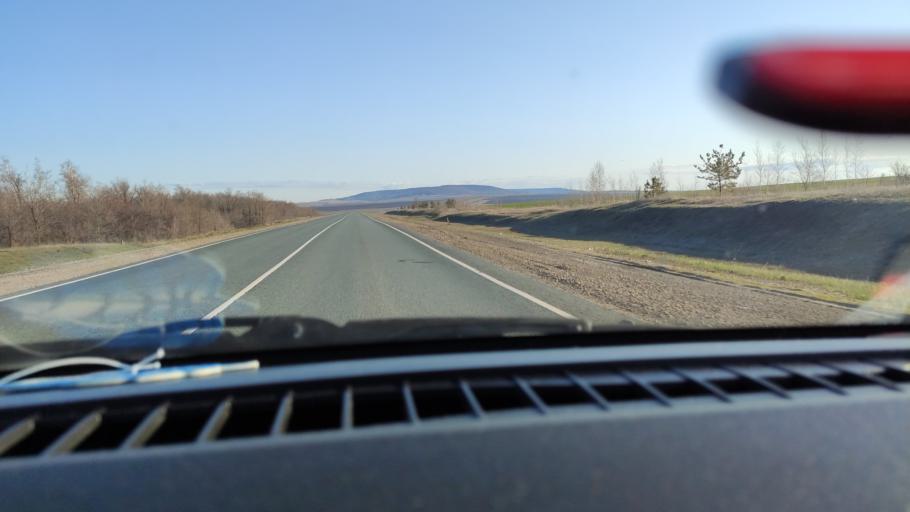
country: RU
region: Saratov
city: Alekseyevka
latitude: 52.2331
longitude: 47.9039
